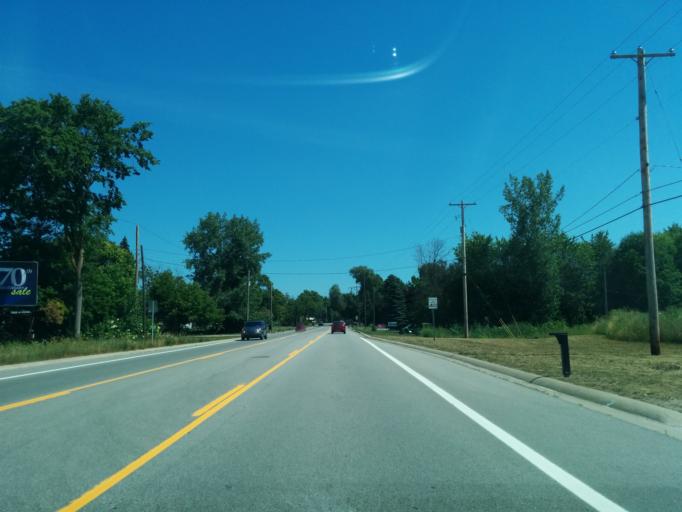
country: US
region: Michigan
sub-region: Bay County
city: Bay City
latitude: 43.5748
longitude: -83.9248
